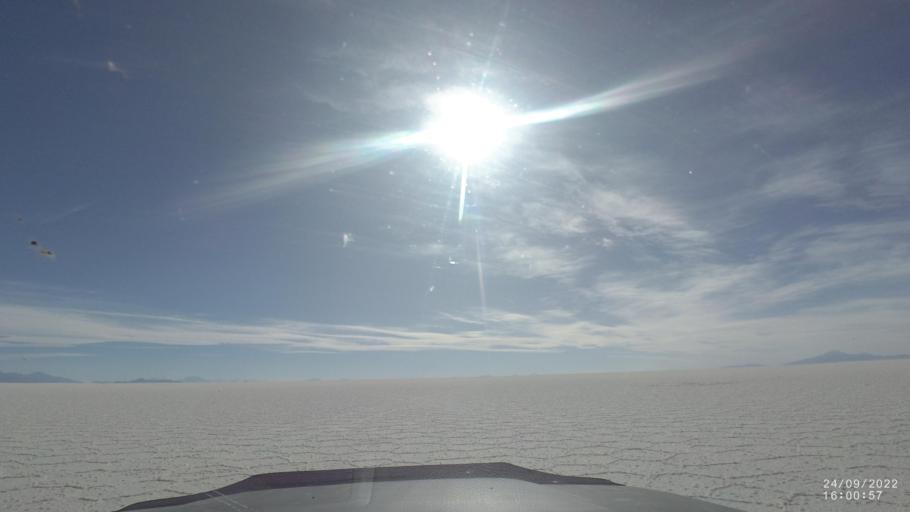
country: BO
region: Potosi
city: Colchani
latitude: -20.3224
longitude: -67.2537
